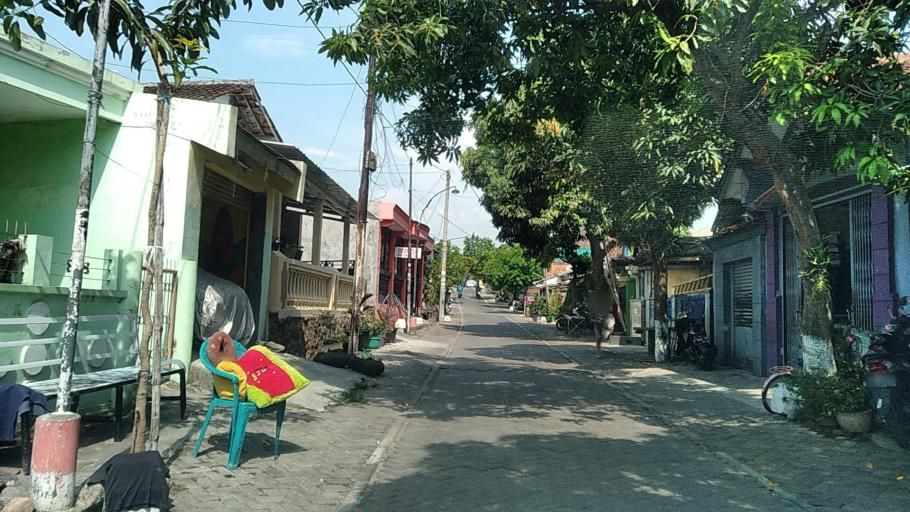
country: ID
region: Central Java
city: Semarang
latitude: -6.9941
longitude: 110.3915
